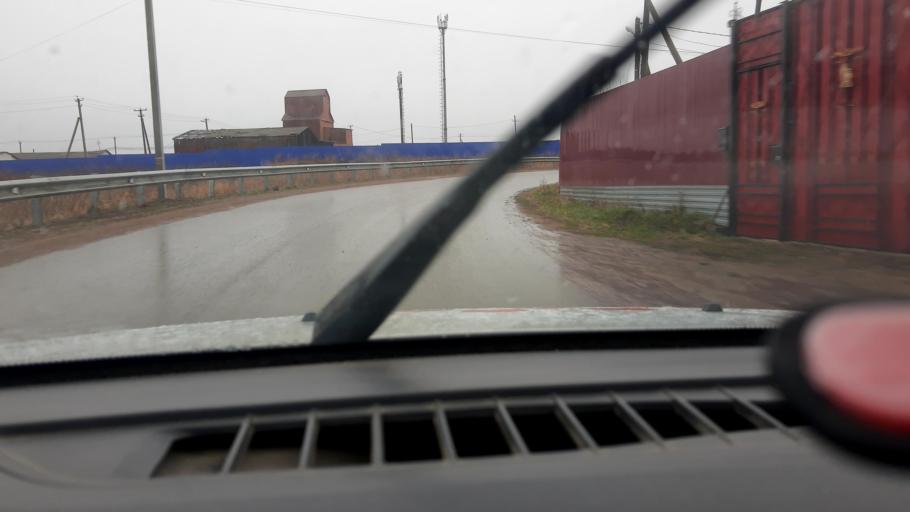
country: RU
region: Bashkortostan
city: Kabakovo
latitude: 54.7085
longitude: 56.2444
